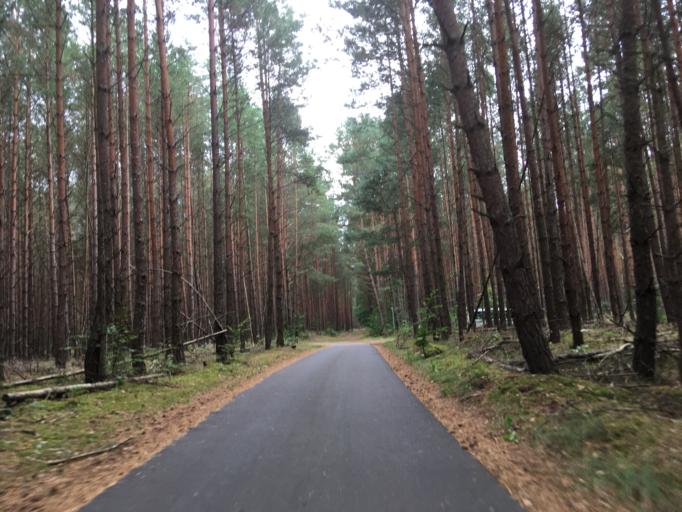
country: DE
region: Brandenburg
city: Friedrichswalde
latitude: 53.0148
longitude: 13.7320
